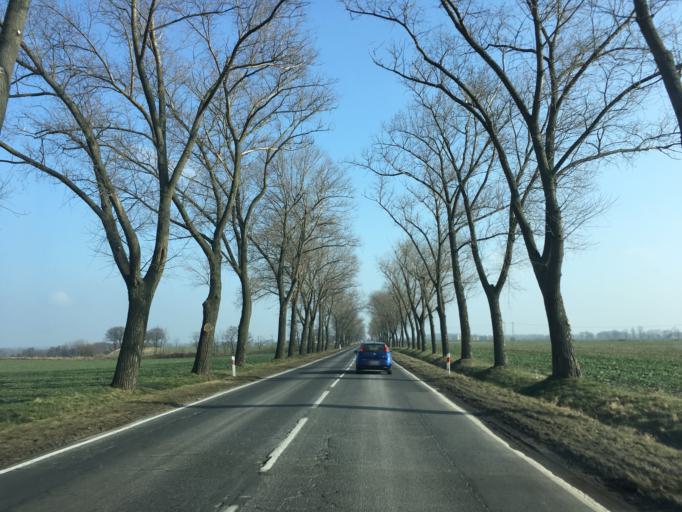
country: PL
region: Lower Silesian Voivodeship
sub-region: Powiat legnicki
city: Chojnow
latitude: 51.2738
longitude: 15.8983
